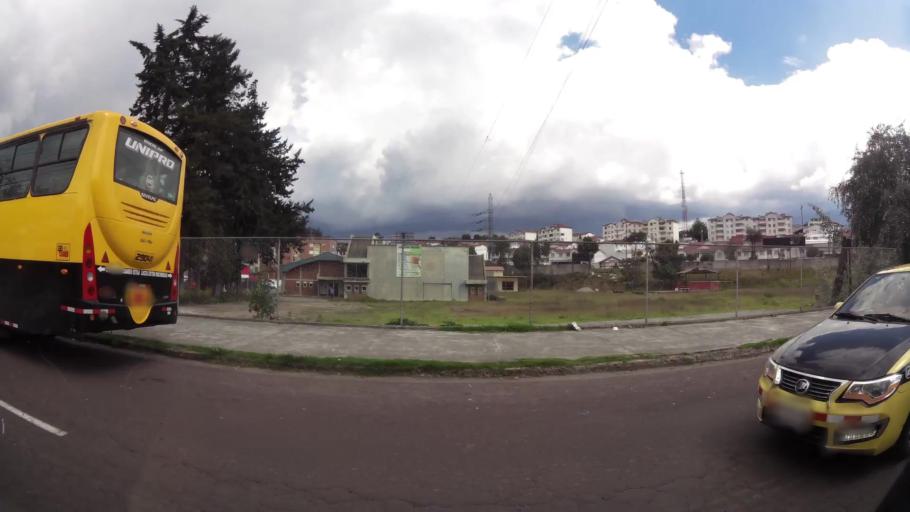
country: EC
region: Pichincha
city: Quito
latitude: -0.0915
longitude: -78.4712
